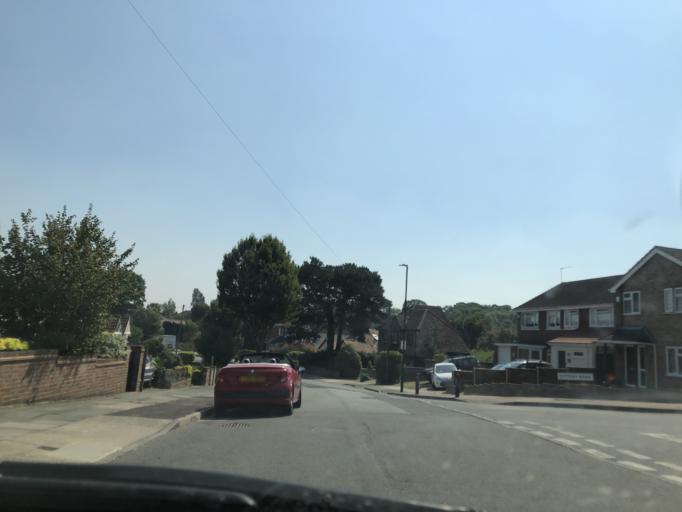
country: GB
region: England
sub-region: Greater London
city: Bexley
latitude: 51.4323
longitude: 0.1635
